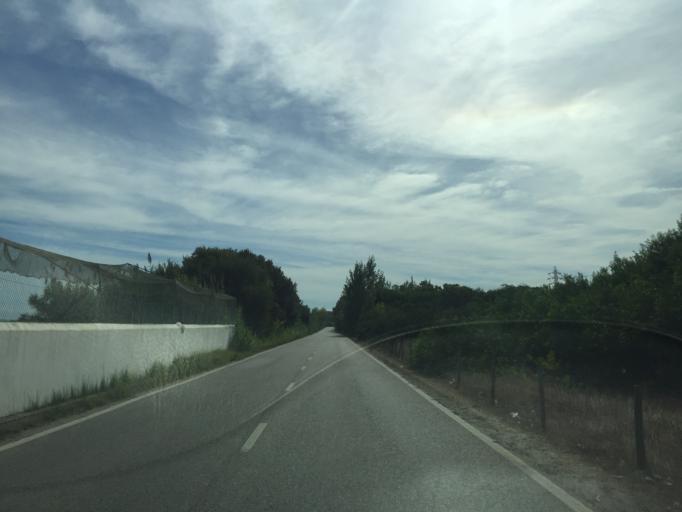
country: PT
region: Coimbra
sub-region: Figueira da Foz
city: Figueira da Foz
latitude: 40.1215
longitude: -8.8491
